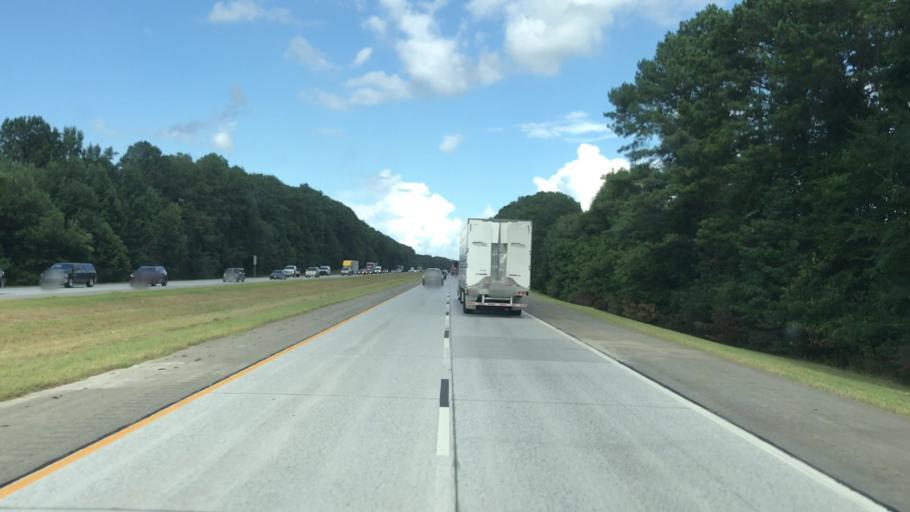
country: US
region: Georgia
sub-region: Morgan County
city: Madison
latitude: 33.5545
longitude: -83.3882
